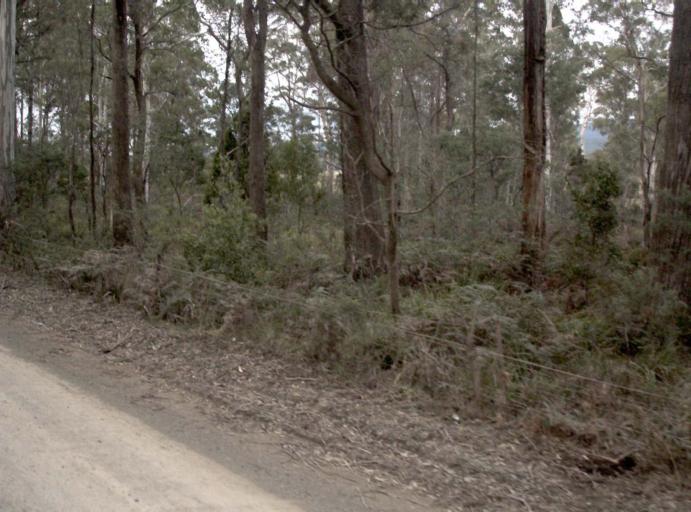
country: AU
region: Tasmania
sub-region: Launceston
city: Newstead
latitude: -41.3624
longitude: 147.2298
